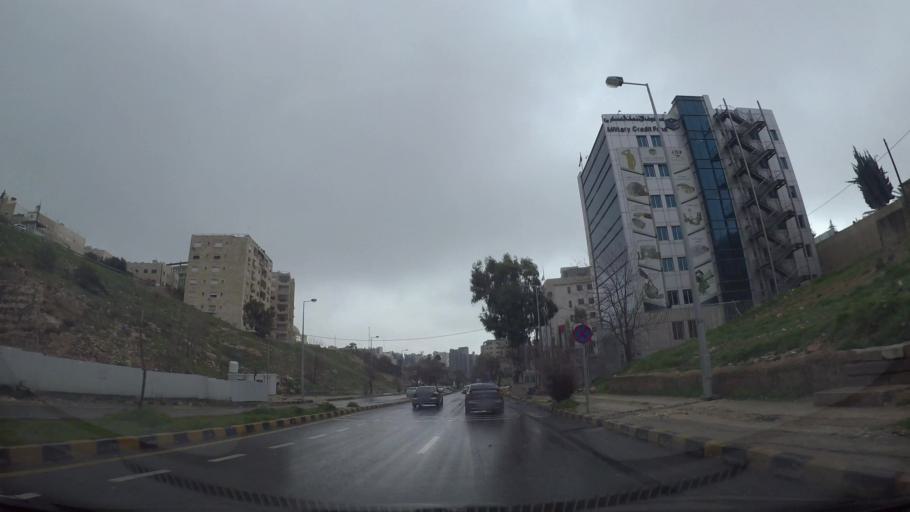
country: JO
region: Amman
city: Amman
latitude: 31.9592
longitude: 35.9020
